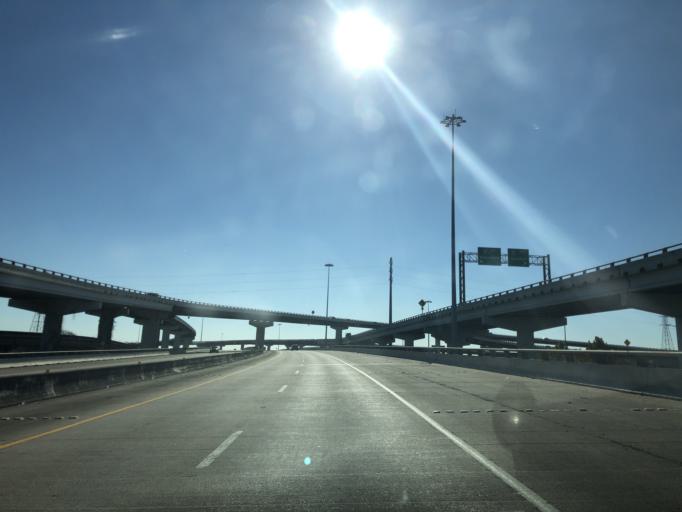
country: US
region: Texas
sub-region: Harris County
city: Cloverleaf
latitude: 29.7755
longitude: -95.1574
